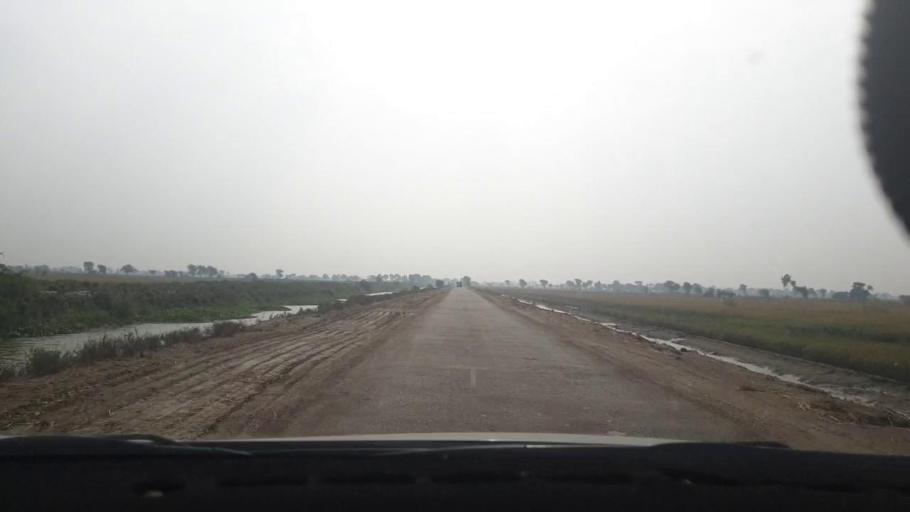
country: PK
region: Sindh
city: Tando Muhammad Khan
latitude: 25.0735
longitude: 68.5357
